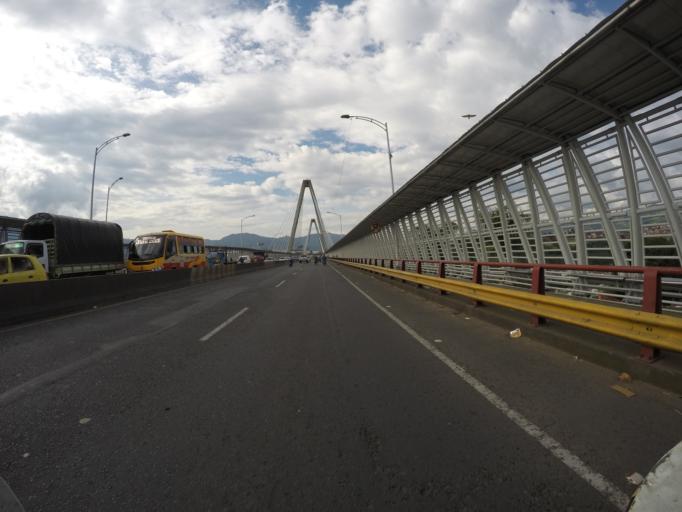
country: CO
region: Risaralda
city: Pereira
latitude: 4.8149
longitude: -75.6870
